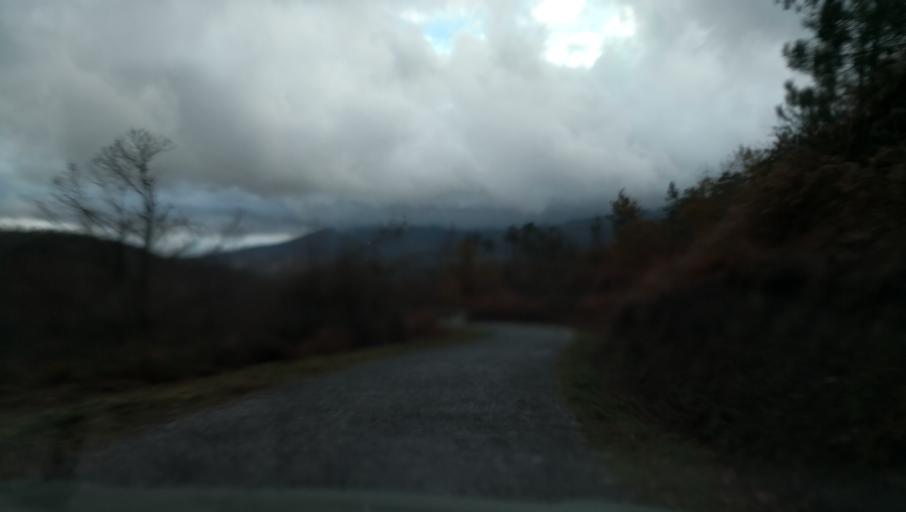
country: PT
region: Vila Real
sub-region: Santa Marta de Penaguiao
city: Santa Marta de Penaguiao
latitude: 41.3086
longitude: -7.8671
